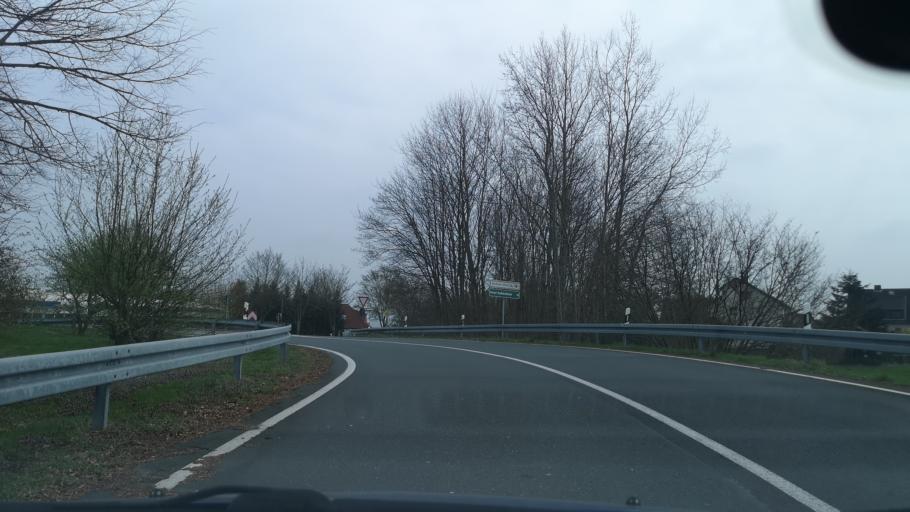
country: DE
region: Lower Saxony
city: Garbsen
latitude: 52.4634
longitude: 9.5321
